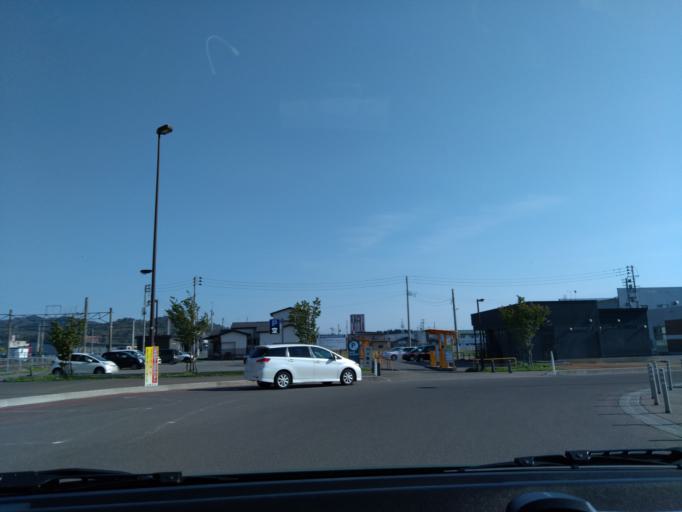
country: JP
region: Akita
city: Yokotemachi
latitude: 39.3101
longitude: 140.5598
